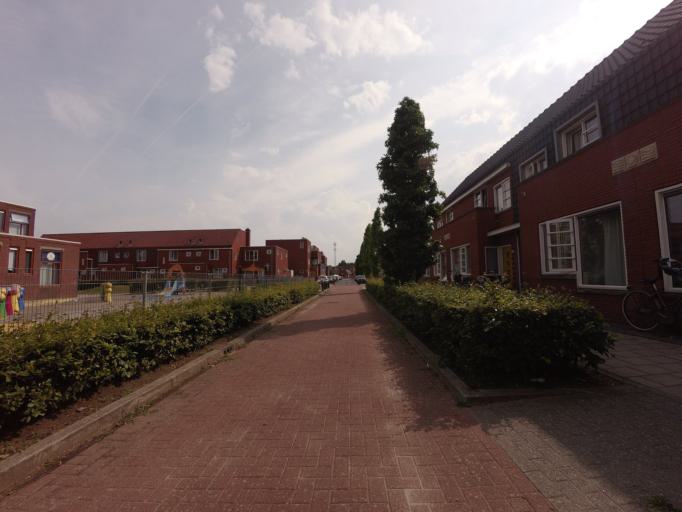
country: NL
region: Flevoland
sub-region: Gemeente Almere
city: Almere Stad
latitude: 52.3719
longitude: 5.2099
